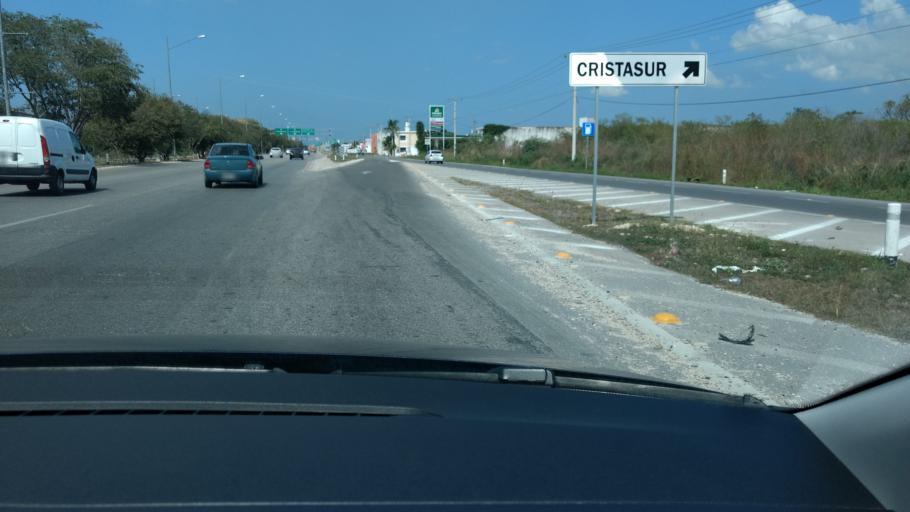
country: MX
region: Yucatan
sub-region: Kanasin
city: Kanasin
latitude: 20.9875
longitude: -89.5628
